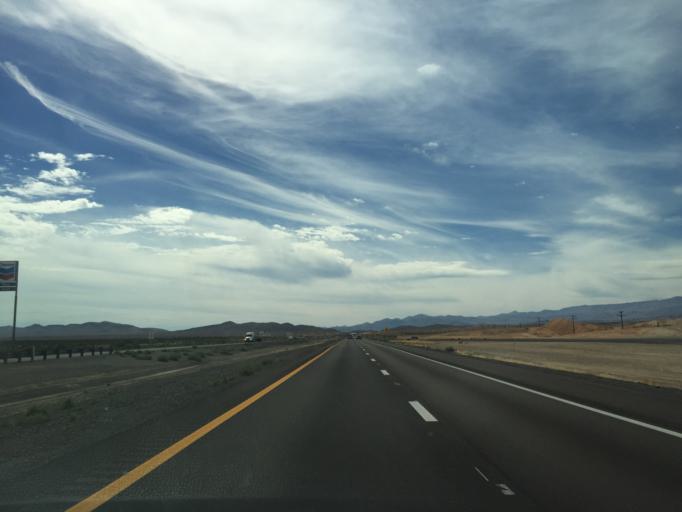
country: US
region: Nevada
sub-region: Clark County
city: Moapa Town
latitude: 36.5021
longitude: -114.7622
